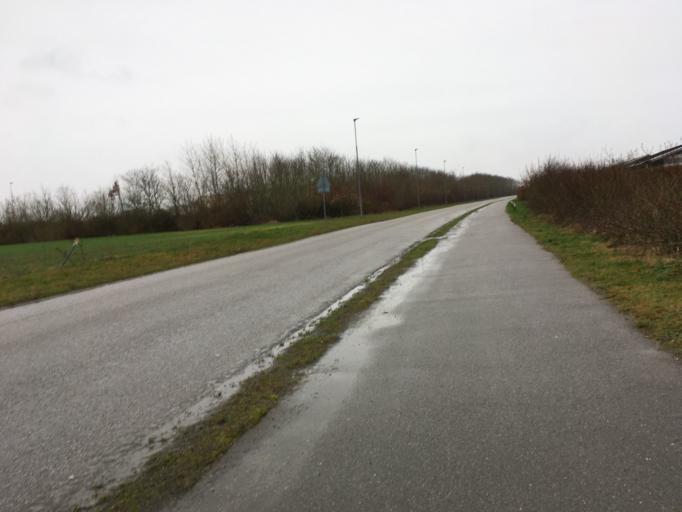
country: DK
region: Central Jutland
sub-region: Ringkobing-Skjern Kommune
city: Ringkobing
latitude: 56.0995
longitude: 8.2685
